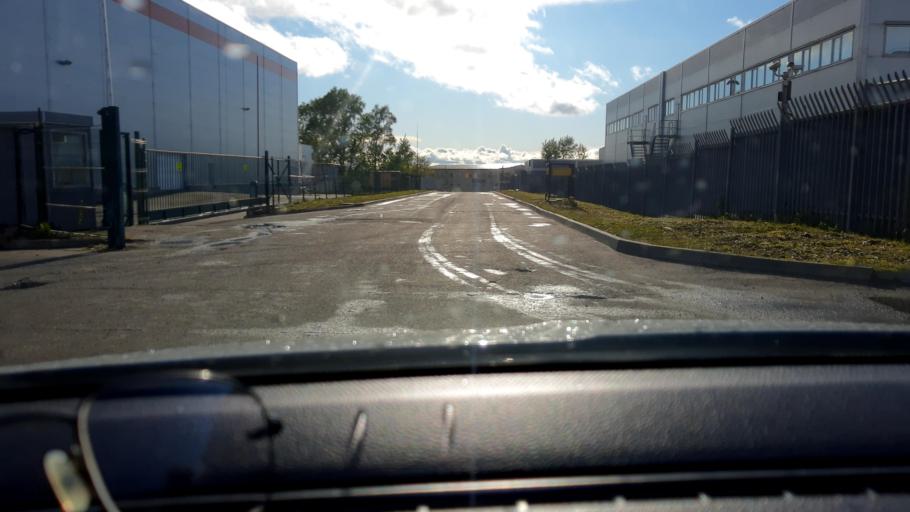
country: RU
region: Moskovskaya
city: Pavlovskaya Sloboda
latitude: 55.8183
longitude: 37.1105
